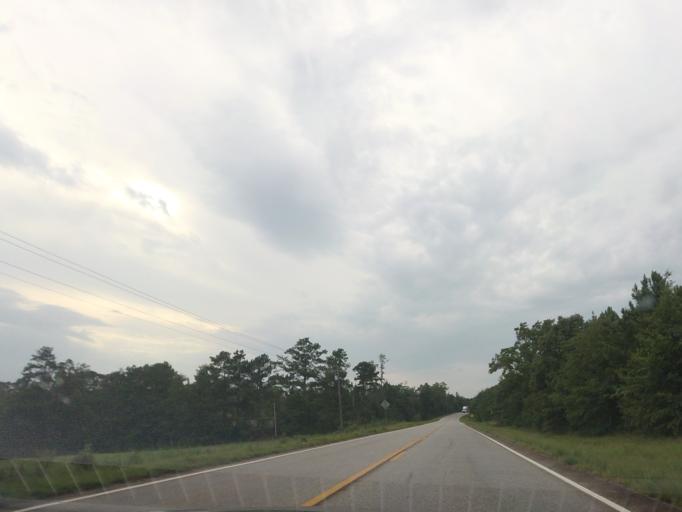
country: US
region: Georgia
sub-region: Twiggs County
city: Jeffersonville
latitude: 32.7209
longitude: -83.4130
